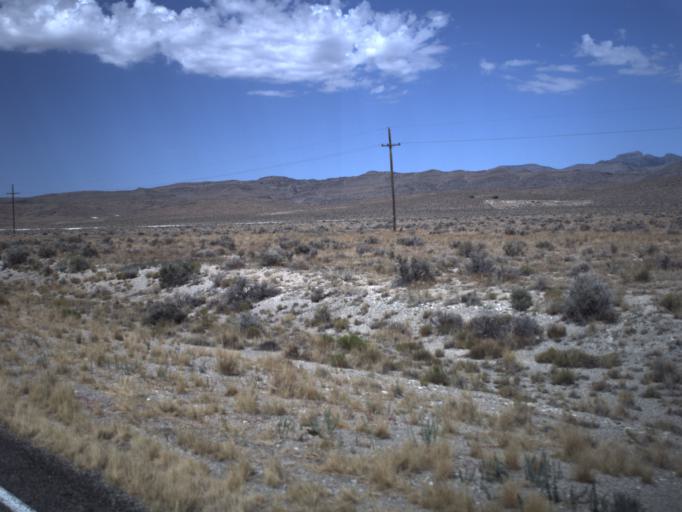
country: US
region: Utah
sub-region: Beaver County
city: Milford
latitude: 39.0679
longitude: -113.2279
